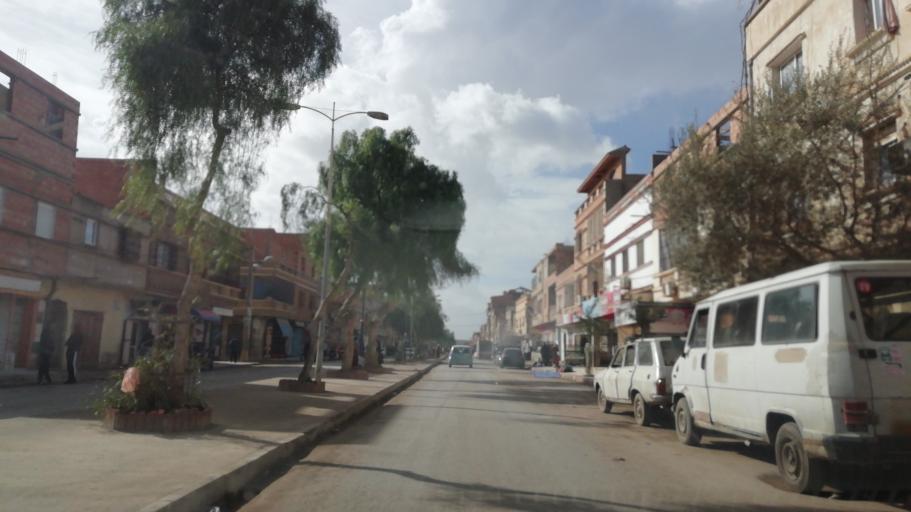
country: DZ
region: Oran
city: Es Senia
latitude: 35.6417
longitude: -0.5738
